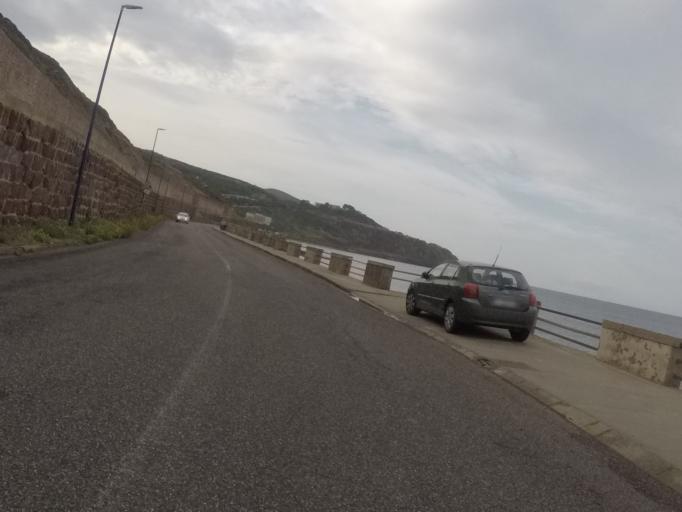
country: IT
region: Sardinia
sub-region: Provincia di Oristano
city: Bosa
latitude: 40.2794
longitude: 8.4838
